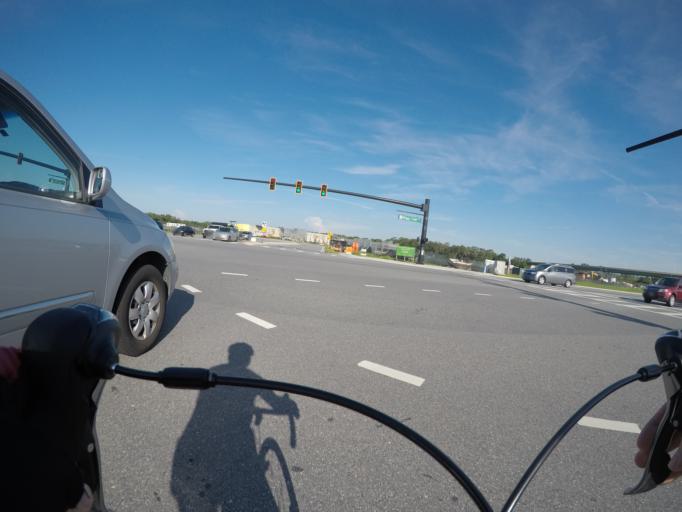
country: US
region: Florida
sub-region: Osceola County
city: Buenaventura Lakes
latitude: 28.3652
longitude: -81.3096
